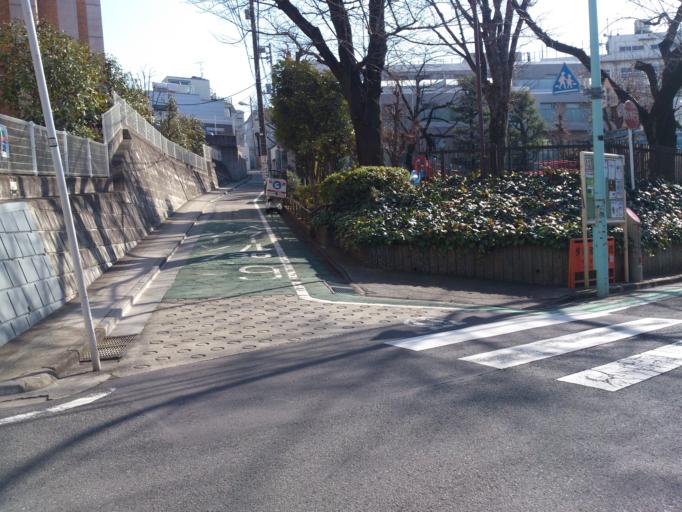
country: JP
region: Tokyo
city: Tokyo
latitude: 35.6672
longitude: 139.6787
